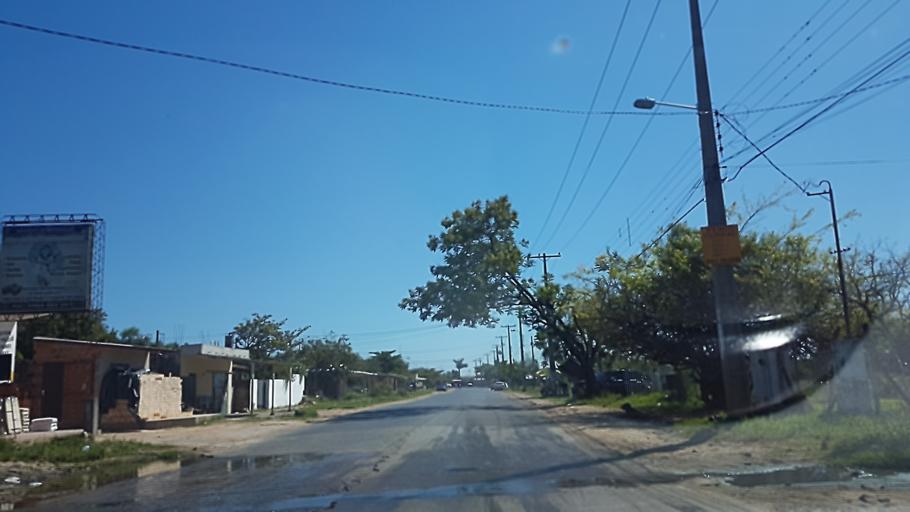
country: PY
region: Central
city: Colonia Mariano Roque Alonso
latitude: -25.2177
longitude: -57.5192
